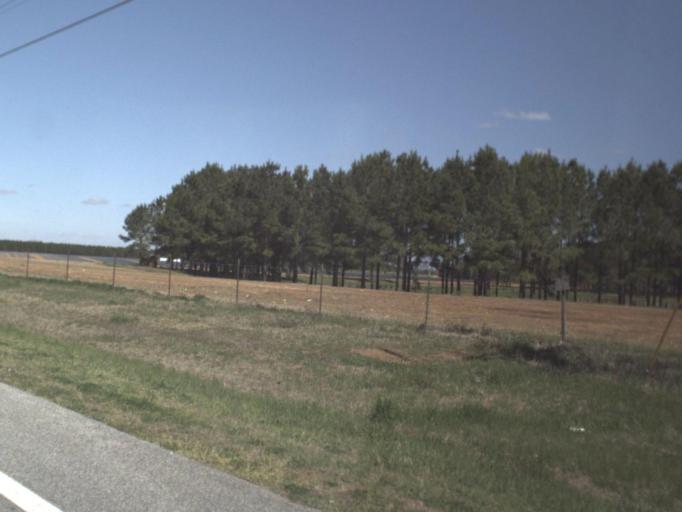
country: US
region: Florida
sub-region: Gadsden County
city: Quincy
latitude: 30.6497
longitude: -84.6012
